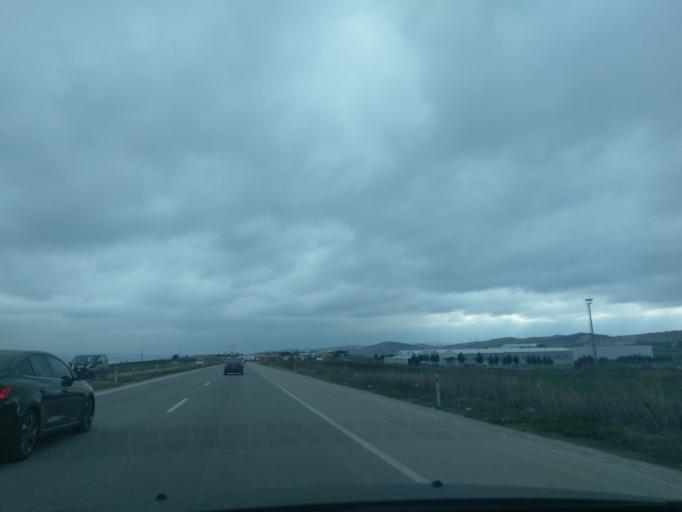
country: TR
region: Istanbul
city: Muratbey
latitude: 41.1101
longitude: 28.5034
